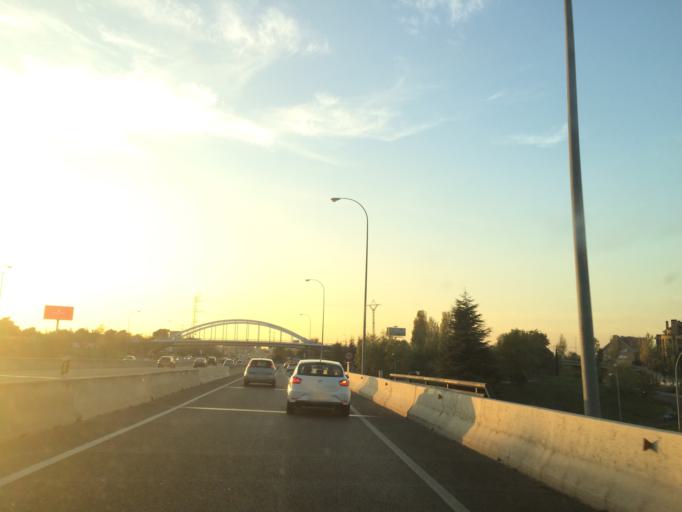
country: ES
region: Madrid
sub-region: Provincia de Madrid
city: Pozuelo de Alarcon
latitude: 40.4649
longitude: -3.7938
